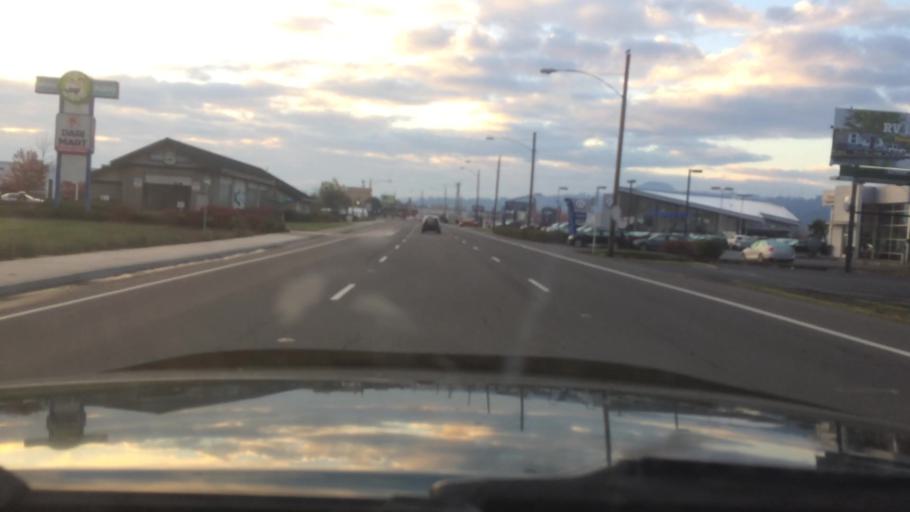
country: US
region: Oregon
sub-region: Lane County
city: Eugene
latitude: 44.0547
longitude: -123.1287
